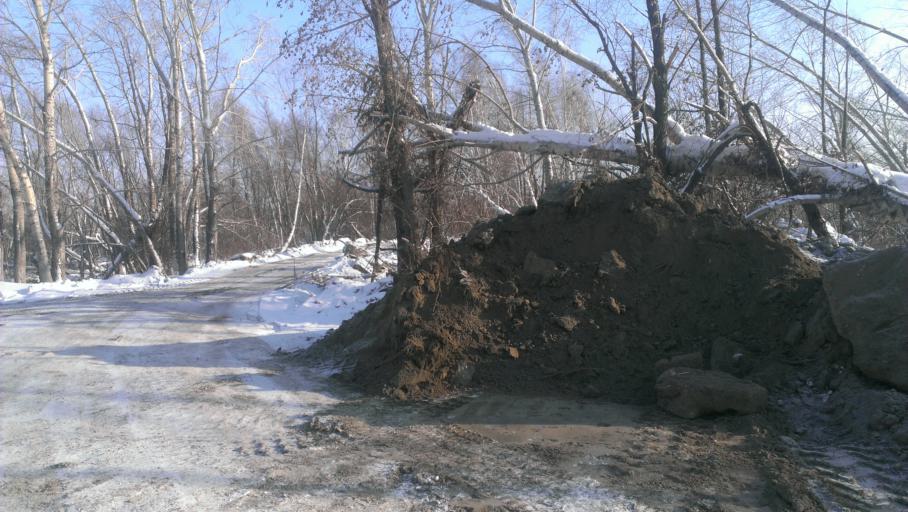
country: RU
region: Altai Krai
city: Zaton
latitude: 53.3178
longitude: 83.8082
